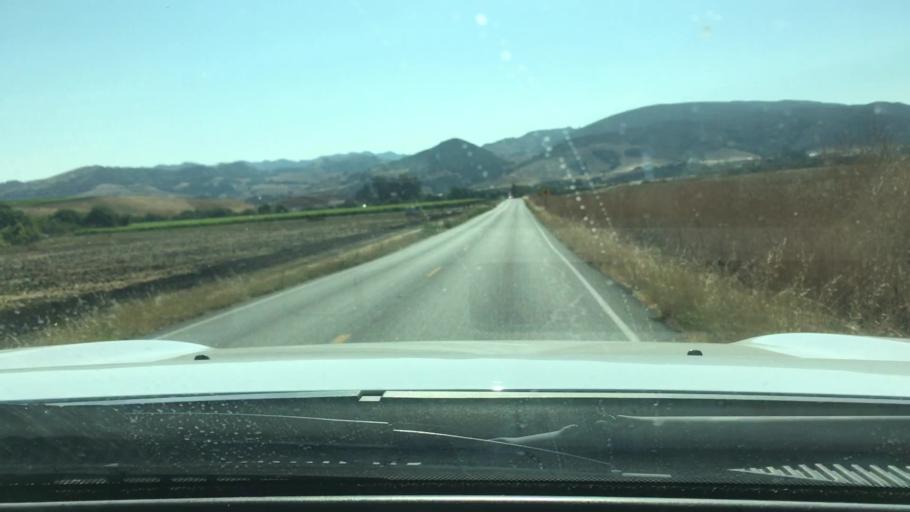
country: US
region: California
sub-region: San Luis Obispo County
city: San Luis Obispo
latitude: 35.2359
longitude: -120.6644
